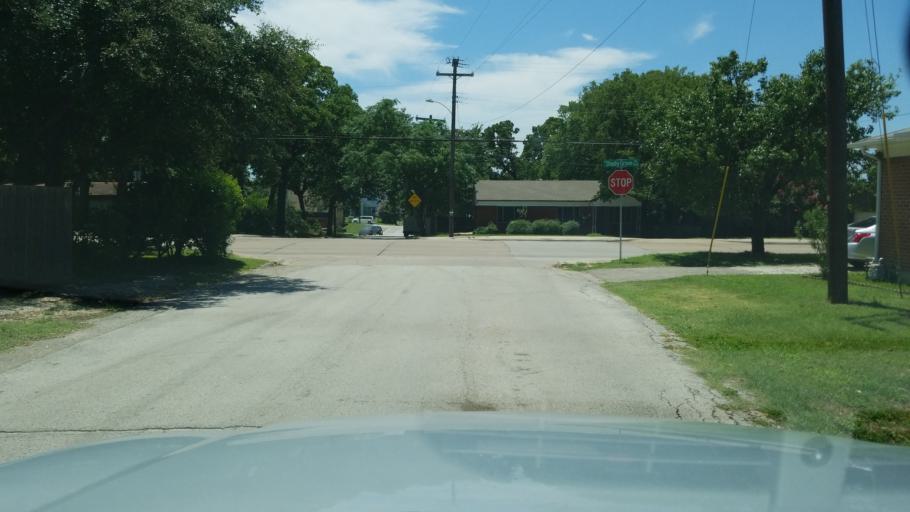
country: US
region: Texas
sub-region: Dallas County
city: Irving
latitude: 32.8016
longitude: -96.9143
